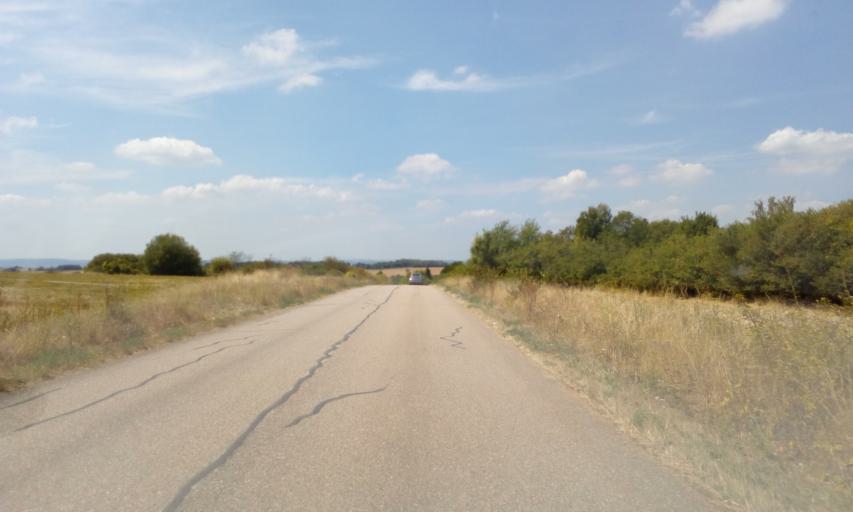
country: FR
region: Lorraine
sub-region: Departement de Meurthe-et-Moselle
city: Pagny-sur-Moselle
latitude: 48.9541
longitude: 5.8807
